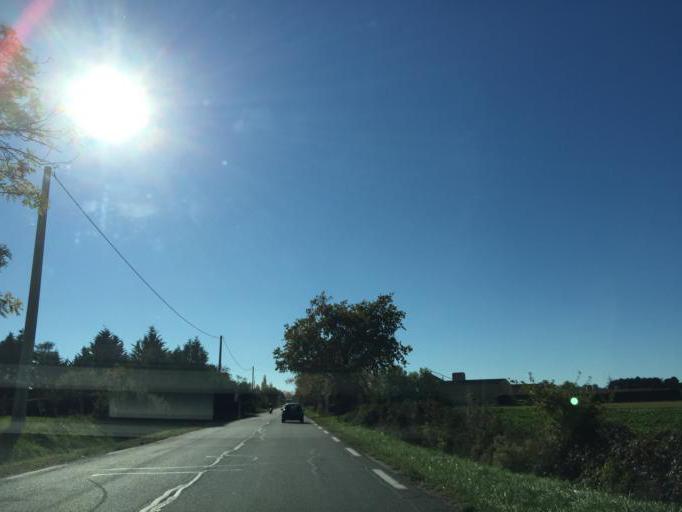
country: FR
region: Rhone-Alpes
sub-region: Departement du Rhone
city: Saint-Maurice-sur-Dargoire
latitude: 45.5804
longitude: 4.6554
